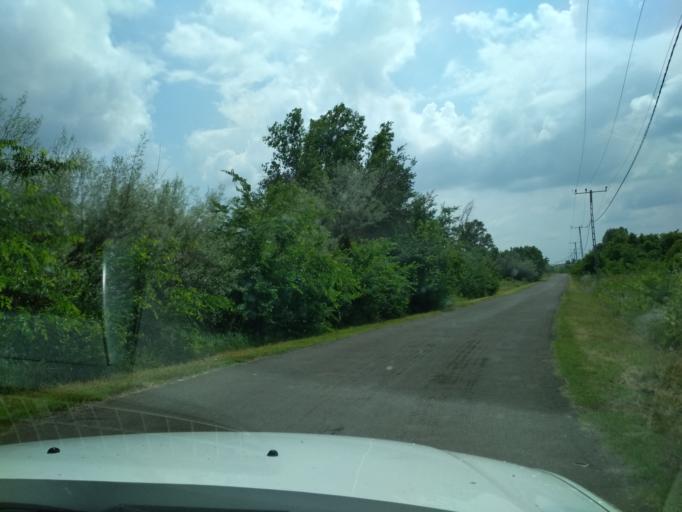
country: HU
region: Pest
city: Nagykata
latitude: 47.3810
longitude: 19.7587
